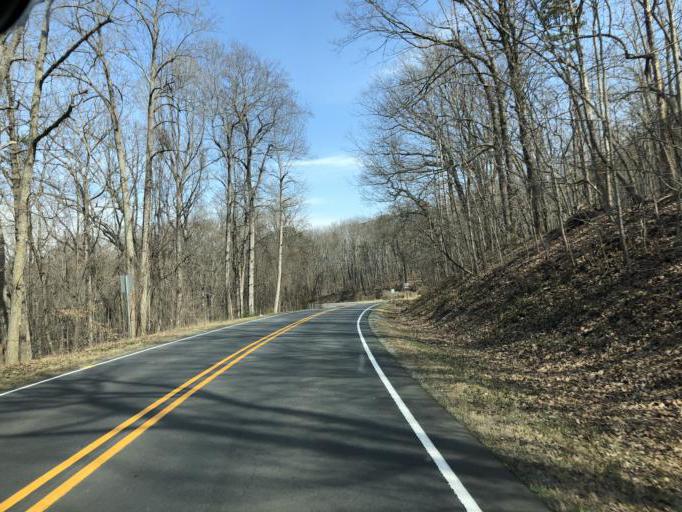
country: US
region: North Carolina
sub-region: Gaston County
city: Ranlo
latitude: 35.3024
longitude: -81.1162
